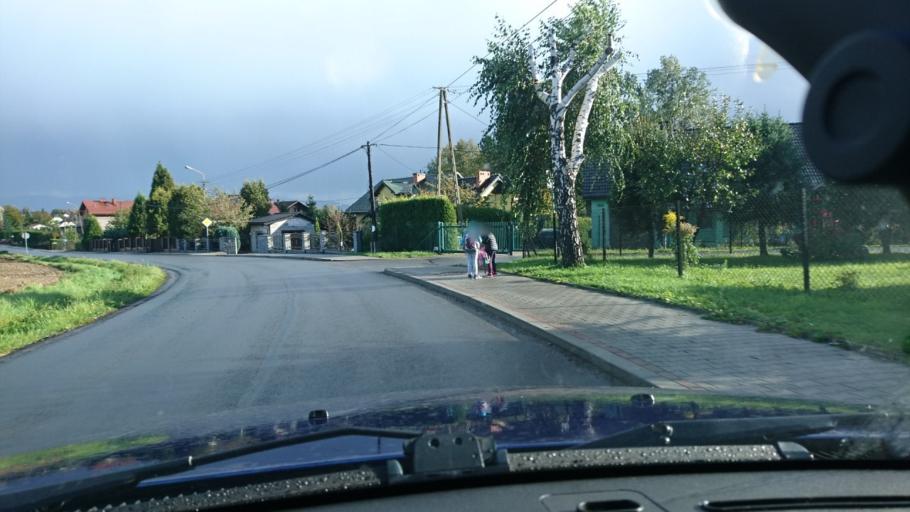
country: PL
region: Silesian Voivodeship
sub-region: Powiat bielski
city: Mazancowice
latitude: 49.8600
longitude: 18.9992
